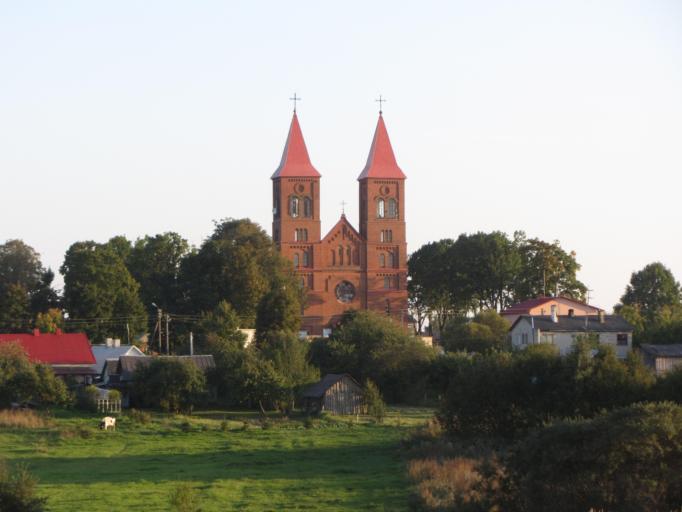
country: LT
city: Eisiskes
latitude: 54.1963
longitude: 24.8437
